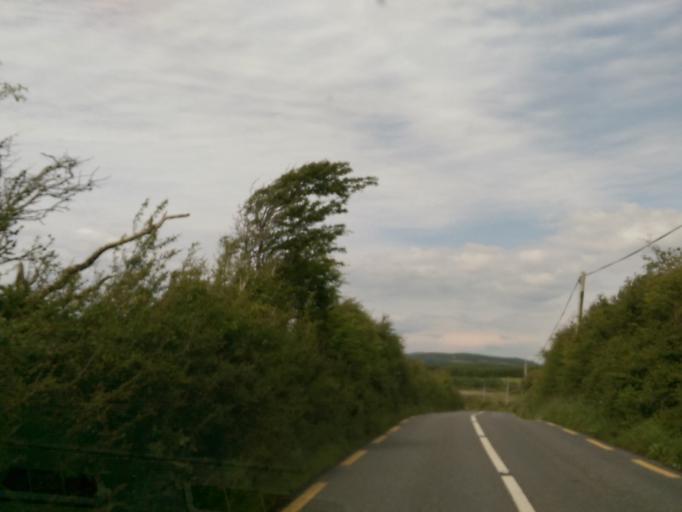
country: IE
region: Connaught
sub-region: County Galway
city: Bearna
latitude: 53.0158
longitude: -9.3094
